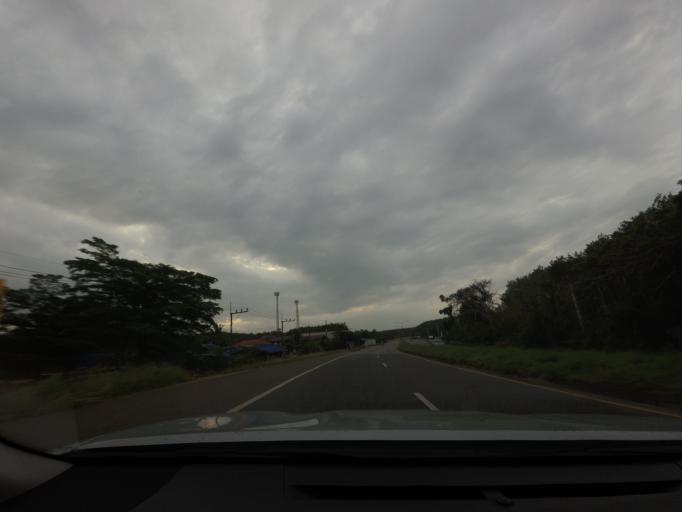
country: TH
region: Surat Thani
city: Phunphin
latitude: 9.0361
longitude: 99.1358
